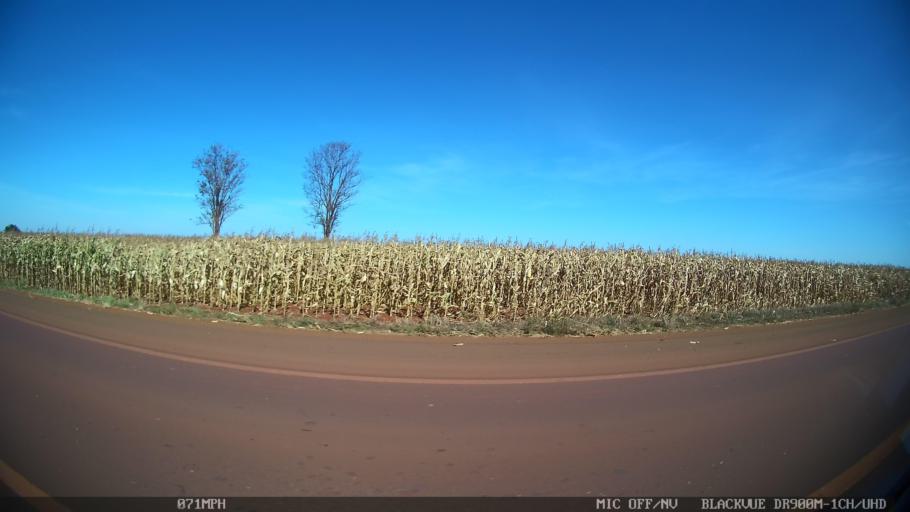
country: BR
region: Sao Paulo
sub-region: Guaira
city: Guaira
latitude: -20.4437
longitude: -48.3376
